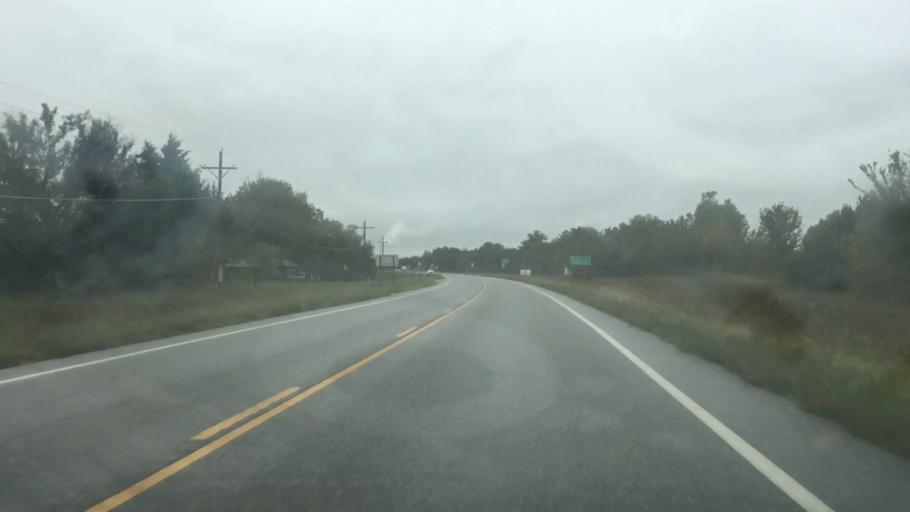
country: US
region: Kansas
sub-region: Anderson County
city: Garnett
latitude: 38.2802
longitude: -95.2214
